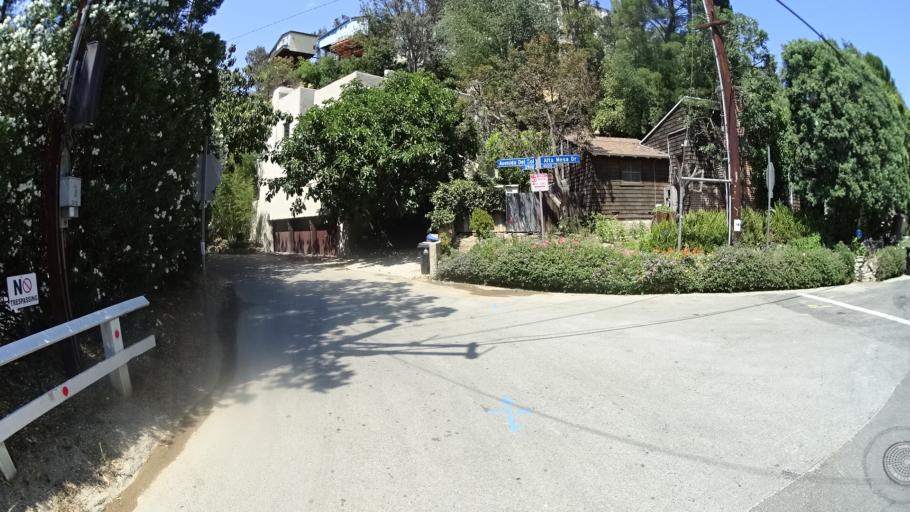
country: US
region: California
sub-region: Los Angeles County
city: Sherman Oaks
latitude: 34.1359
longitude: -118.4113
